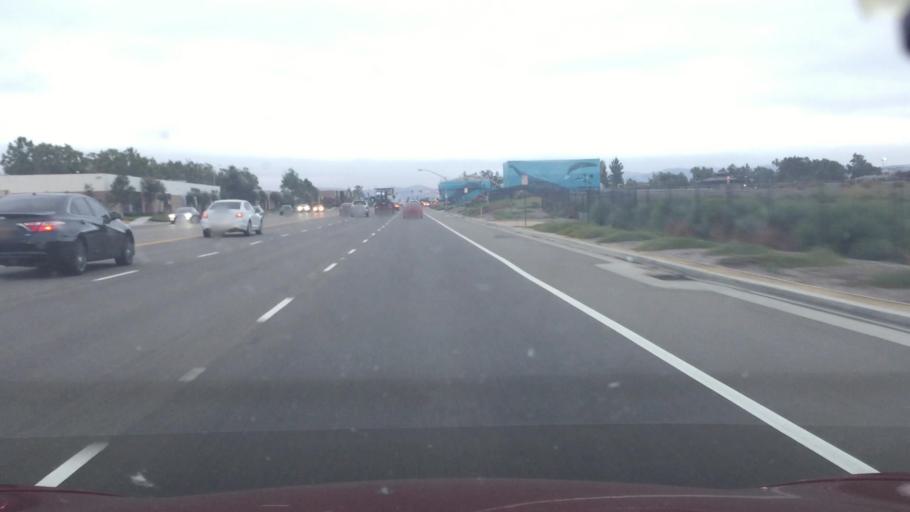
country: US
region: California
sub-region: Alameda County
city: Livermore
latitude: 37.6936
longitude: -121.8059
